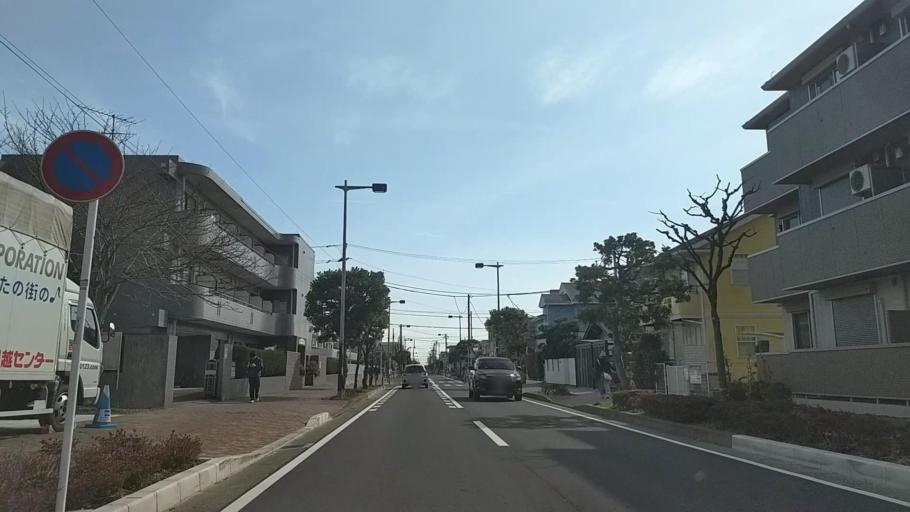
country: JP
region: Kanagawa
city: Fujisawa
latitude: 35.3322
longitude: 139.4474
